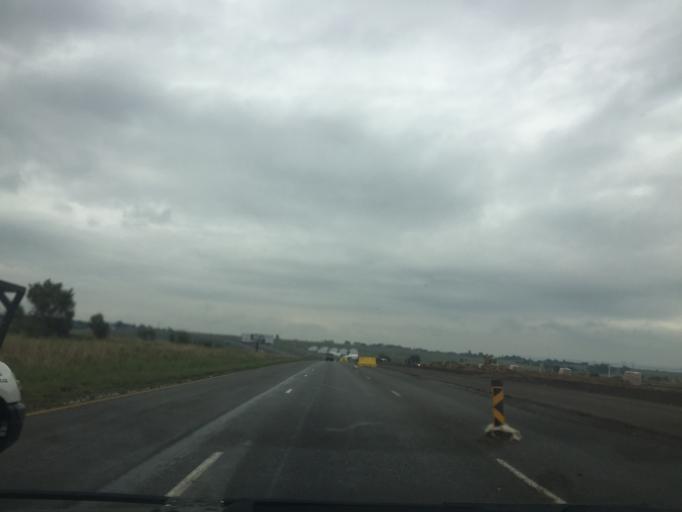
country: ZA
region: Gauteng
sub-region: City of Johannesburg Metropolitan Municipality
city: Diepsloot
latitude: -25.9043
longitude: 28.0501
